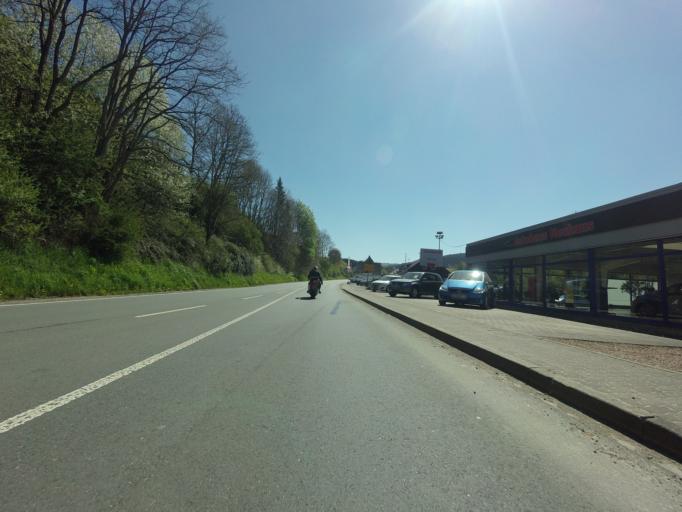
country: DE
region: North Rhine-Westphalia
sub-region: Regierungsbezirk Arnsberg
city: Kirchhundem
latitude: 51.0888
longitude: 8.1157
